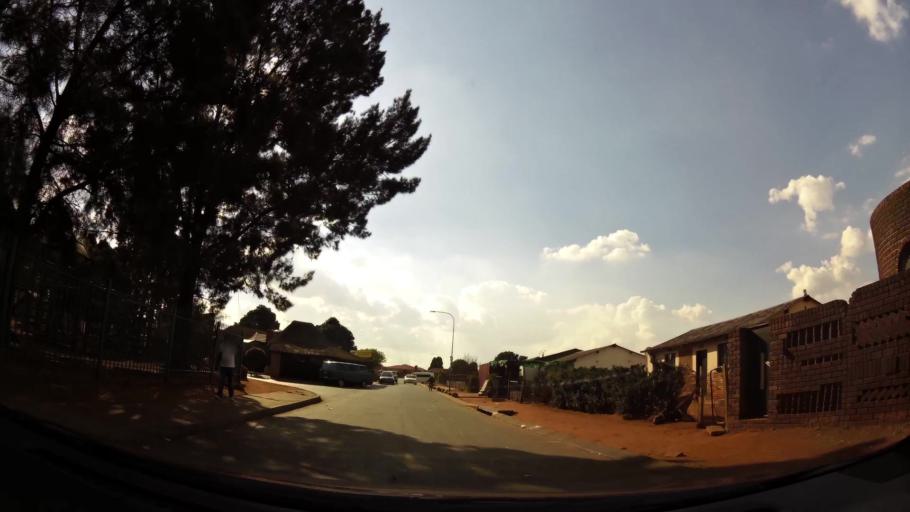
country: ZA
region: Gauteng
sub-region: City of Johannesburg Metropolitan Municipality
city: Soweto
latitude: -26.2215
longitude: 27.8629
